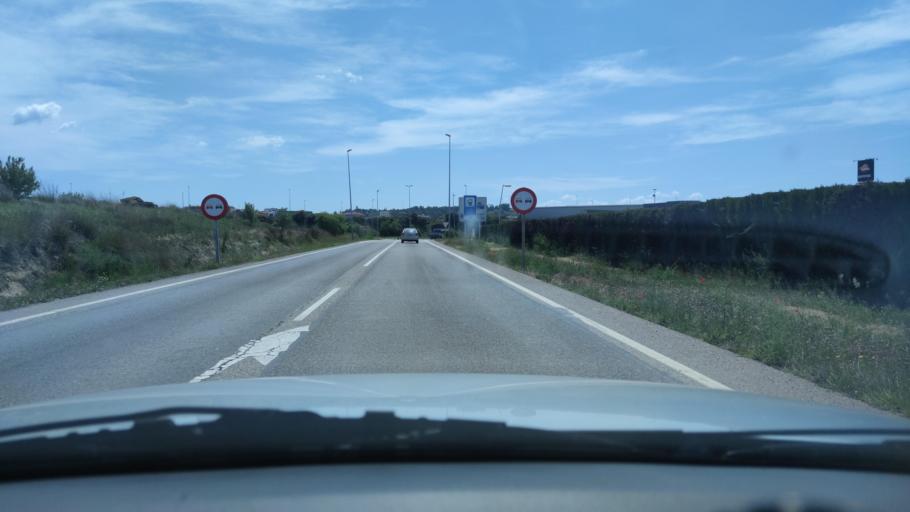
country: ES
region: Catalonia
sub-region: Provincia de Lleida
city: Tarrega
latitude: 41.6639
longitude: 1.1387
